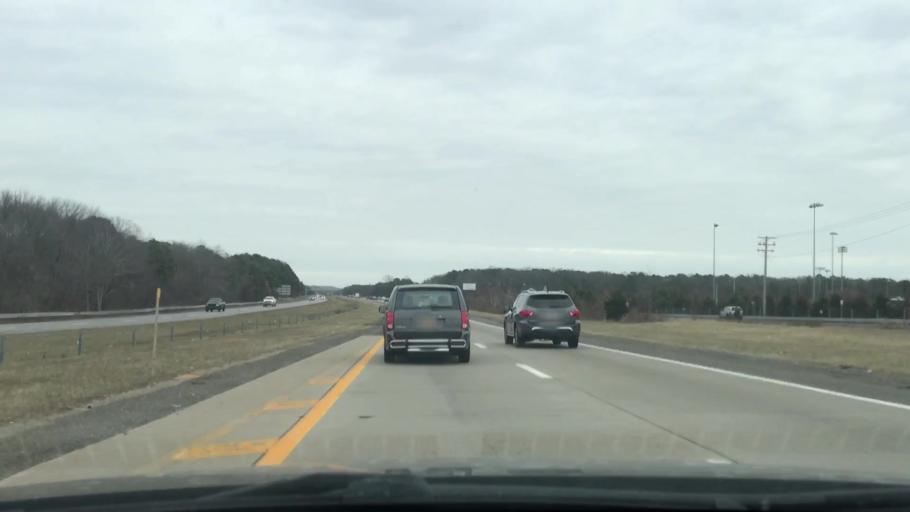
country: US
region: New York
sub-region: Suffolk County
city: East Patchogue
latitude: 40.7806
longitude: -72.9943
